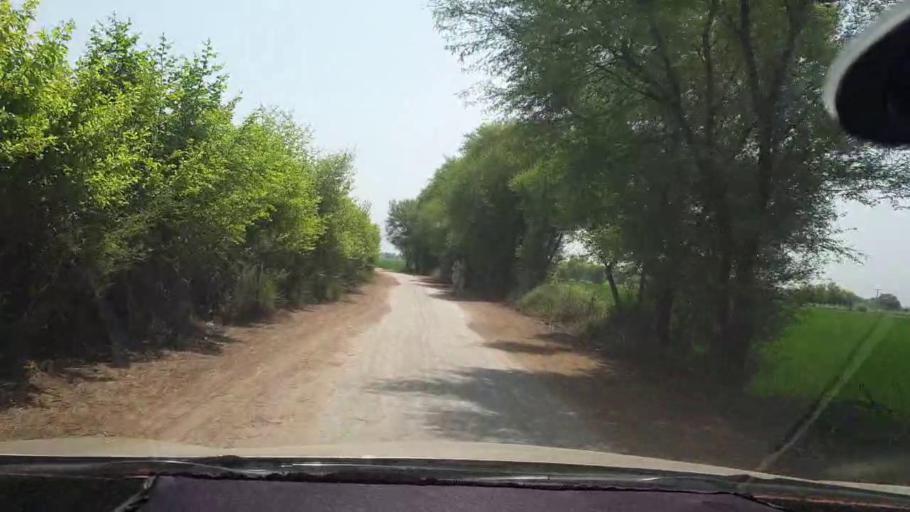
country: PK
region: Sindh
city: Kambar
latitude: 27.6615
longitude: 67.9324
